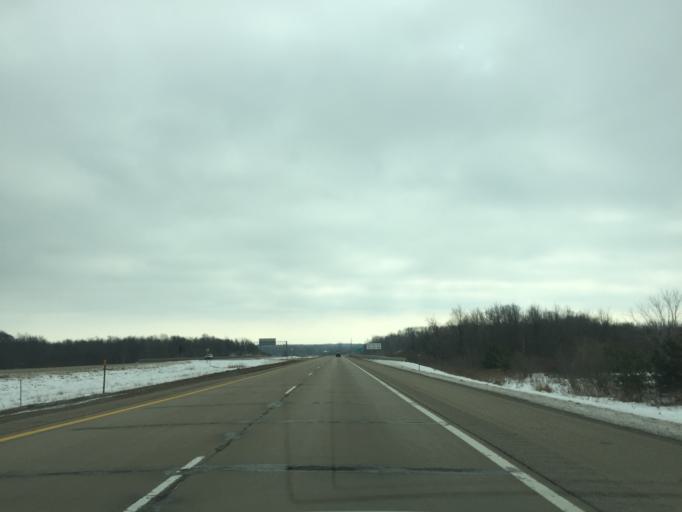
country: US
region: Michigan
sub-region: Ottawa County
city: Hudsonville
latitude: 42.8545
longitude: -85.8126
